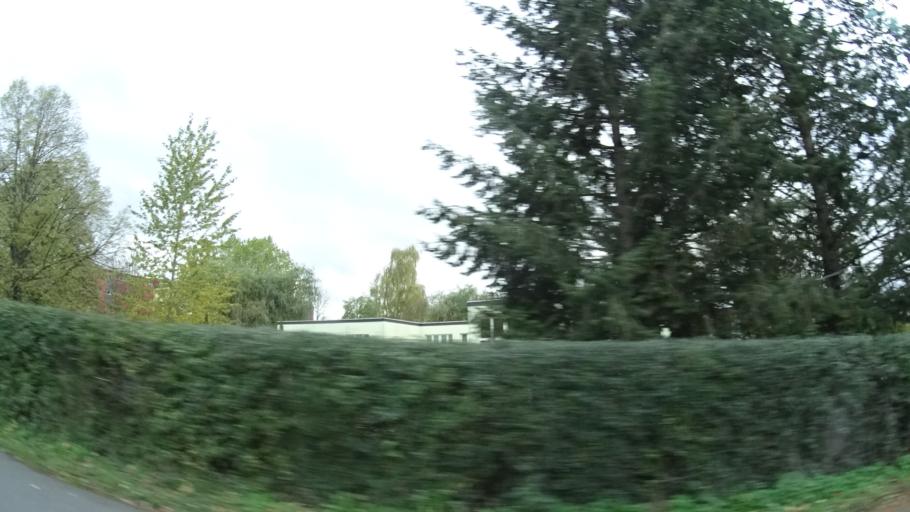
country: DE
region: Thuringia
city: Bodelwitz
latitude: 50.6987
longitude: 11.6155
